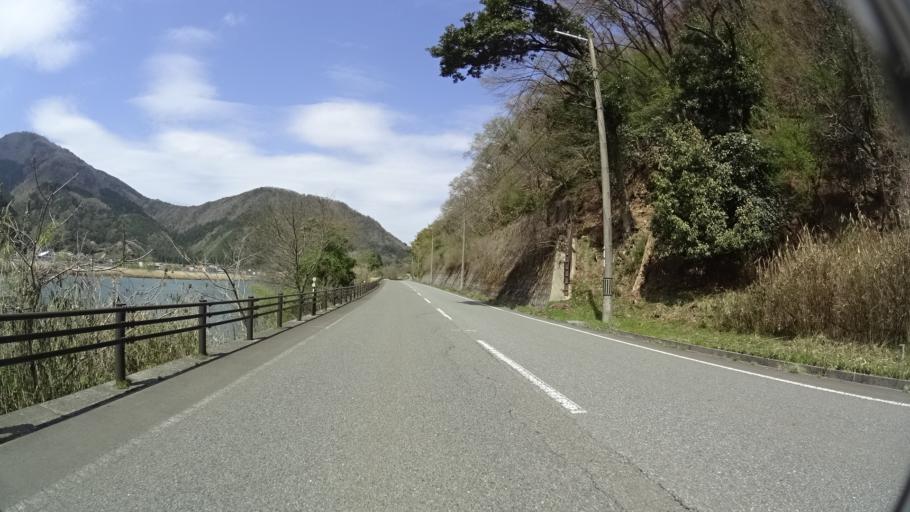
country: JP
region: Hyogo
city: Toyooka
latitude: 35.6006
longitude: 134.8059
